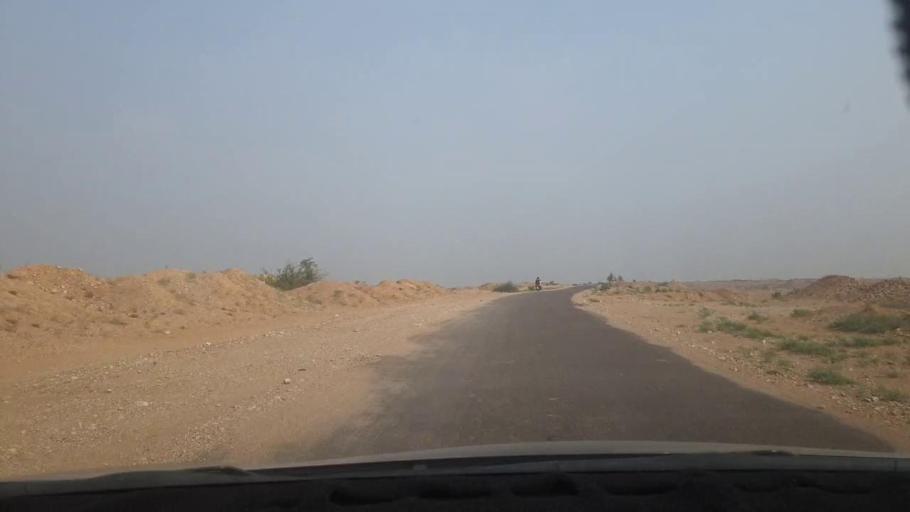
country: PK
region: Sindh
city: Matiari
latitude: 25.5780
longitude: 68.3209
